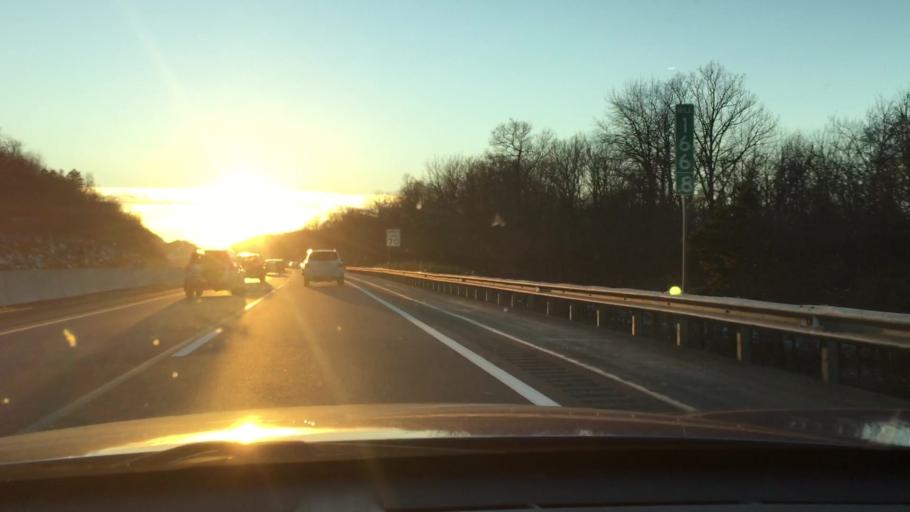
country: US
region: Pennsylvania
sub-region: Bedford County
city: Earlston
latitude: 40.0282
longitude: -78.1746
